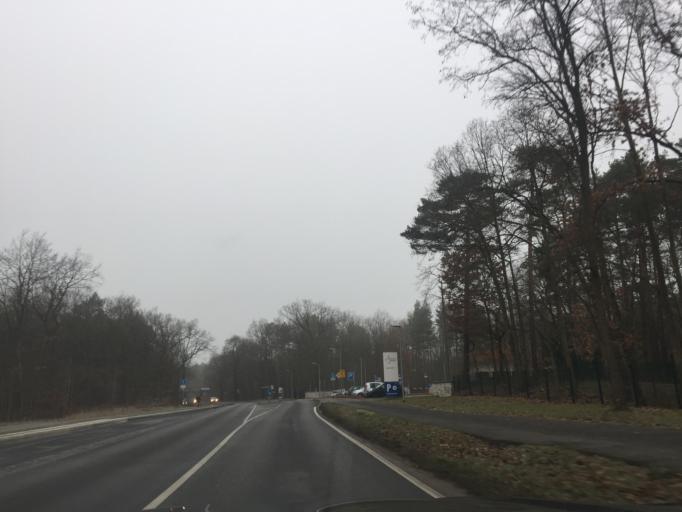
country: DE
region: Brandenburg
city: Hennigsdorf
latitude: 52.6551
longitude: 13.1888
